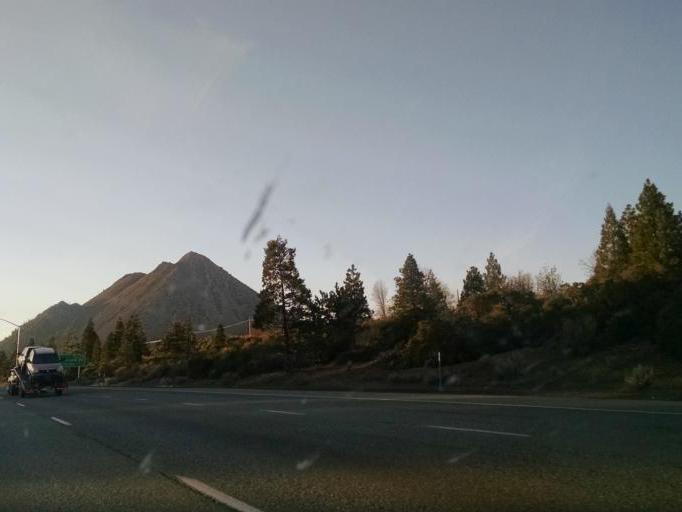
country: US
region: California
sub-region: Siskiyou County
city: Mount Shasta
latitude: 41.3332
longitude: -122.3330
